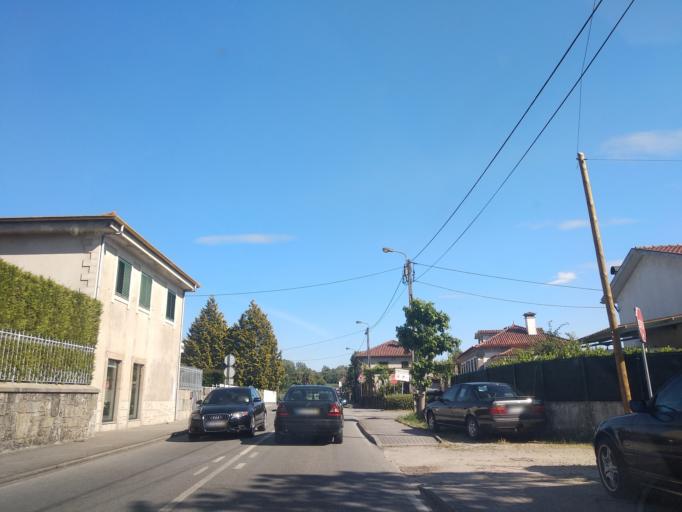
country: PT
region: Braga
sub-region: Vila Verde
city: Prado
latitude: 41.5943
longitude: -8.4619
